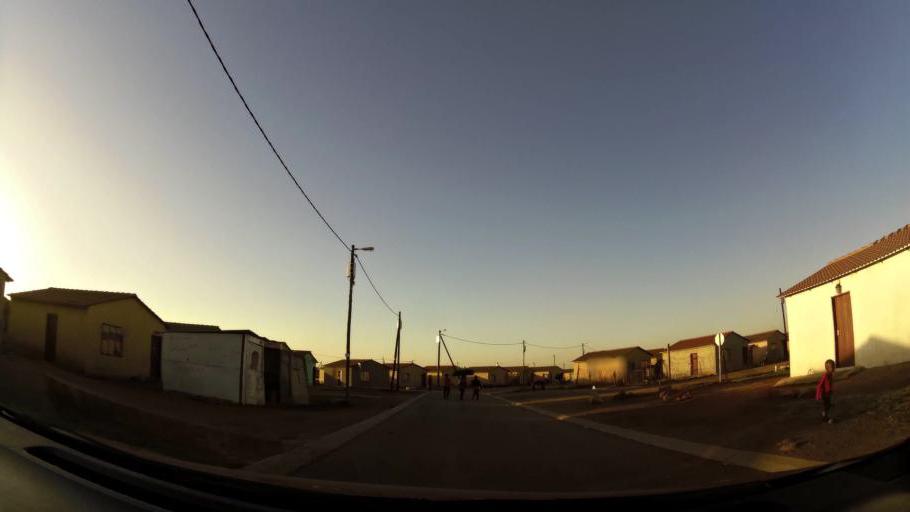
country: ZA
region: North-West
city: Ga-Rankuwa
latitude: -25.6035
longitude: 28.0989
